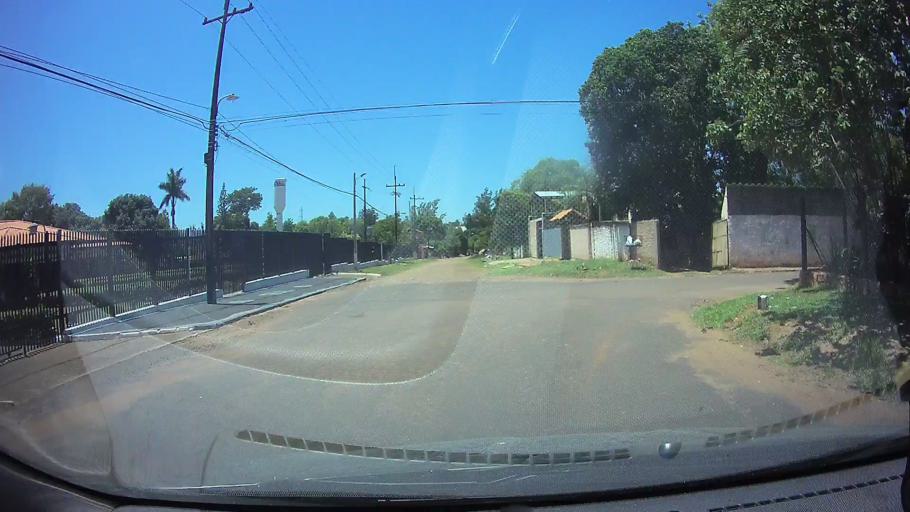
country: PY
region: Central
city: San Lorenzo
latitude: -25.3530
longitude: -57.4888
